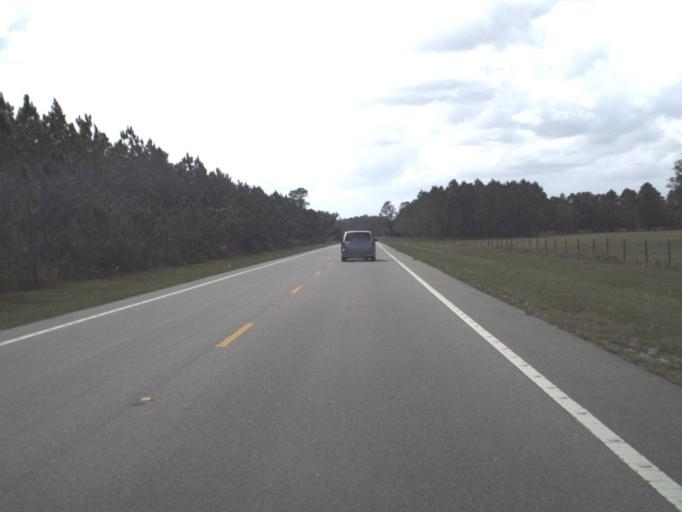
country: US
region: Florida
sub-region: Putnam County
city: Crescent City
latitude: 29.4884
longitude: -81.4670
